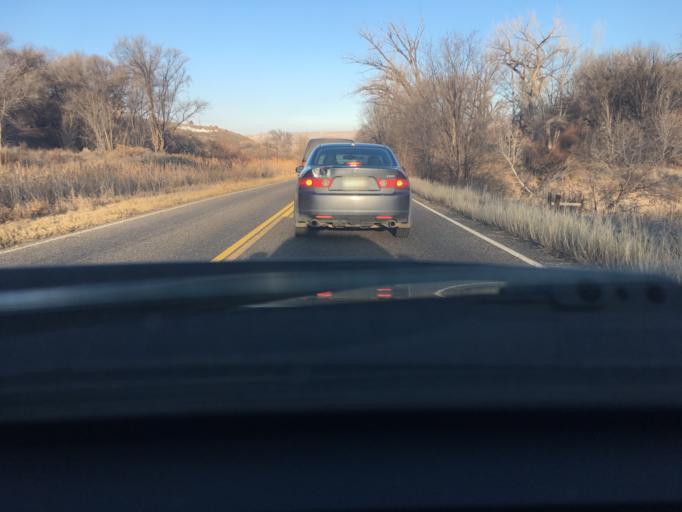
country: US
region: Colorado
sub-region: Delta County
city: Delta
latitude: 38.7446
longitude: -108.1149
